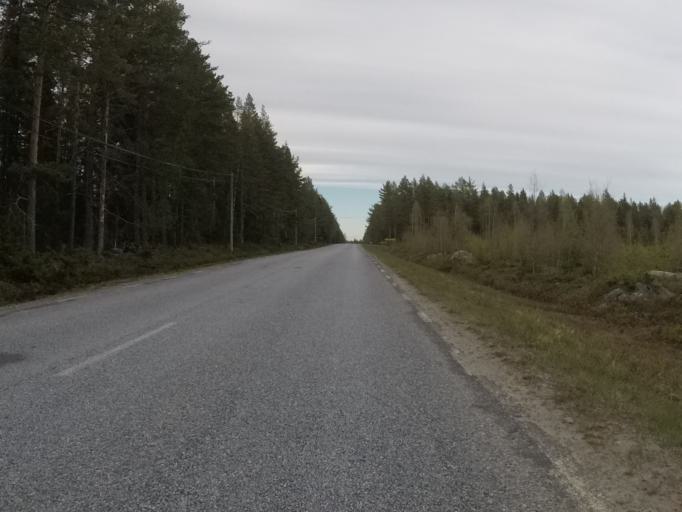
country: SE
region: Vaesterbotten
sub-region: Umea Kommun
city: Saevar
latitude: 63.9243
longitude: 20.7714
